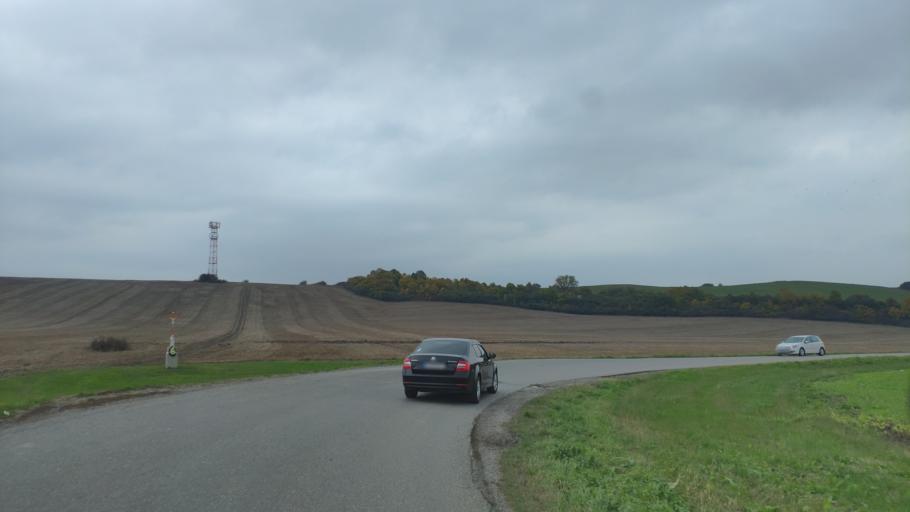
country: SK
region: Kosicky
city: Kosice
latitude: 48.6392
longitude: 21.3733
